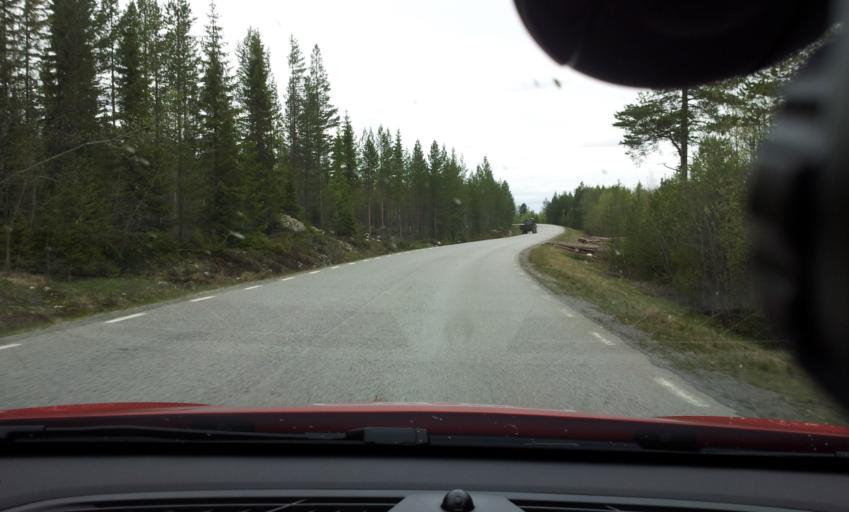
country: SE
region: Jaemtland
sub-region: Bergs Kommun
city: Hoverberg
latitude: 62.7554
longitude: 14.5661
